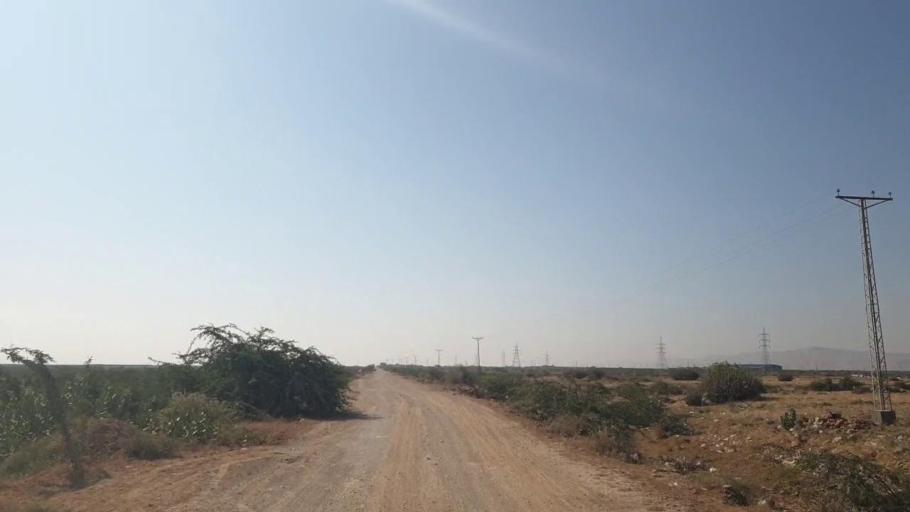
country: PK
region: Sindh
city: Gharo
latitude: 25.1632
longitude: 67.7282
